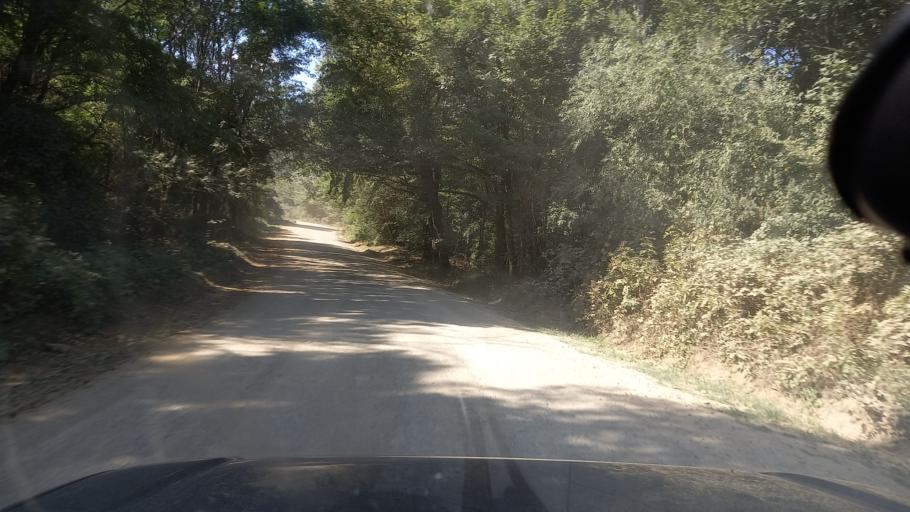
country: RU
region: Krasnodarskiy
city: Azovskaya
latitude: 44.6977
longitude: 38.6533
